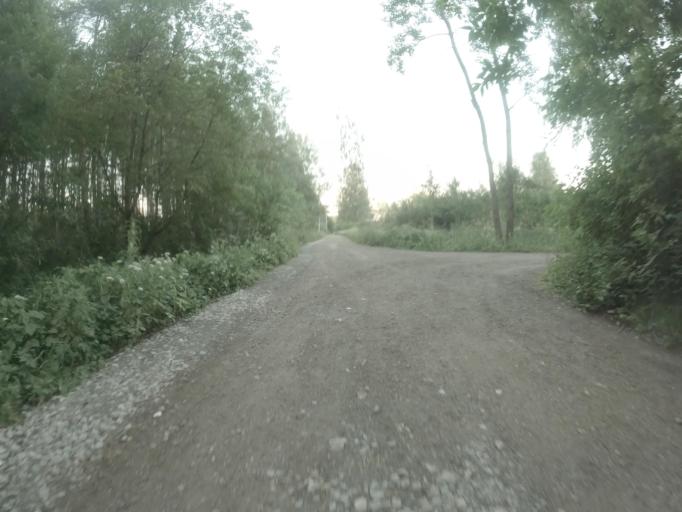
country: RU
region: St.-Petersburg
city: Krasnogvargeisky
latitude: 59.9539
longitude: 30.5055
